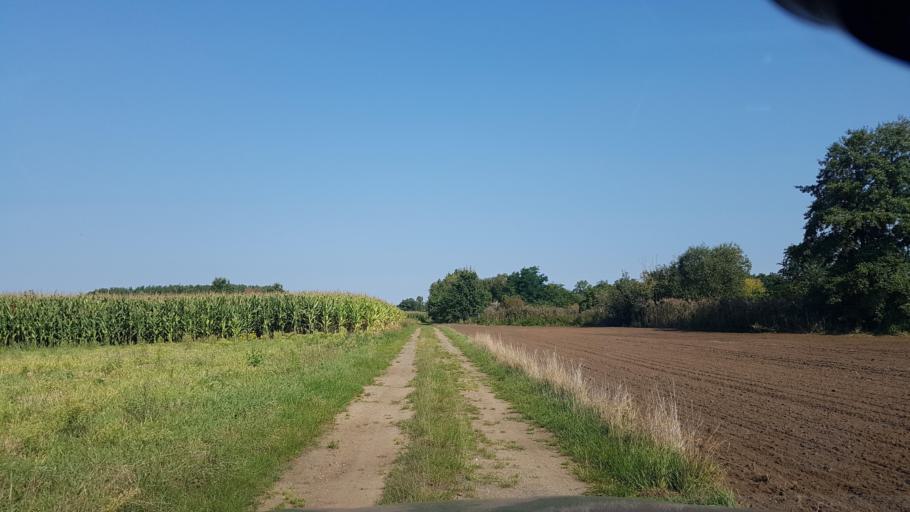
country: DE
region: Brandenburg
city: Bad Liebenwerda
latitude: 51.4998
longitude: 13.4112
